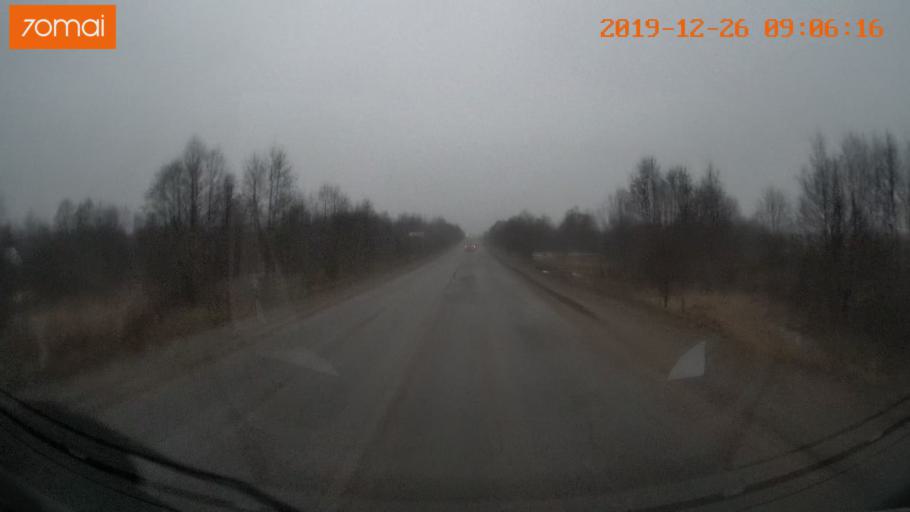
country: RU
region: Vologda
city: Gryazovets
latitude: 58.8343
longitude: 40.2540
